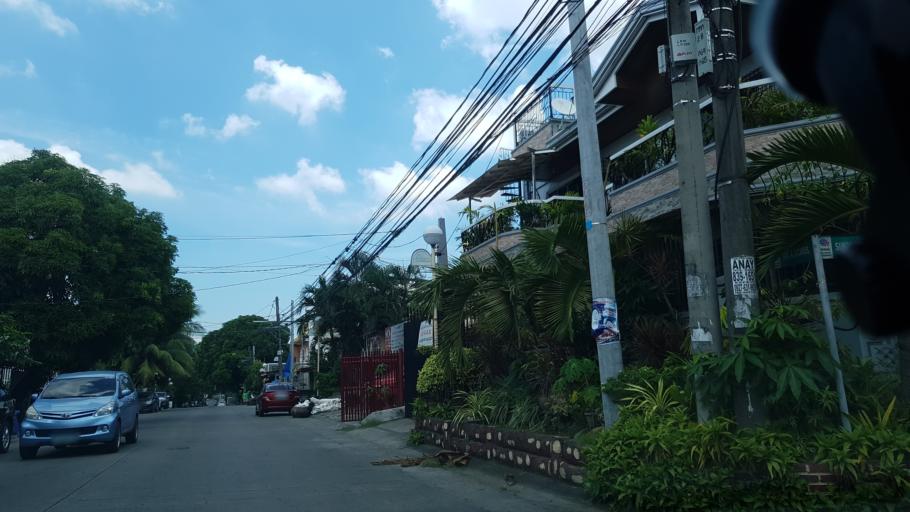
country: PH
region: Calabarzon
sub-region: Province of Rizal
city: Las Pinas
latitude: 14.4311
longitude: 120.9885
